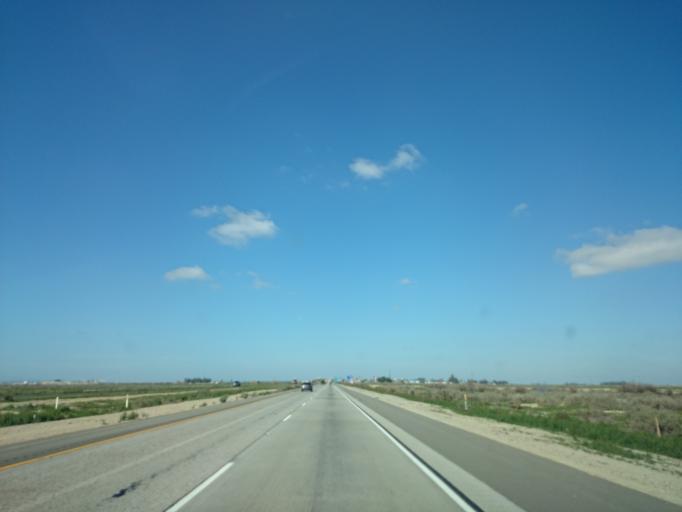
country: US
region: California
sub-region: Kern County
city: Buttonwillow
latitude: 35.3887
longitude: -119.3831
